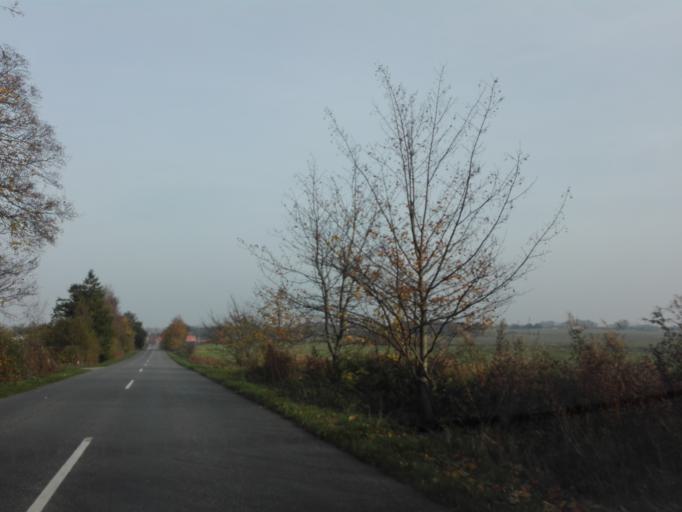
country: DK
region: Central Jutland
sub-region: Arhus Kommune
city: Solbjerg
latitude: 56.0345
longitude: 10.0738
